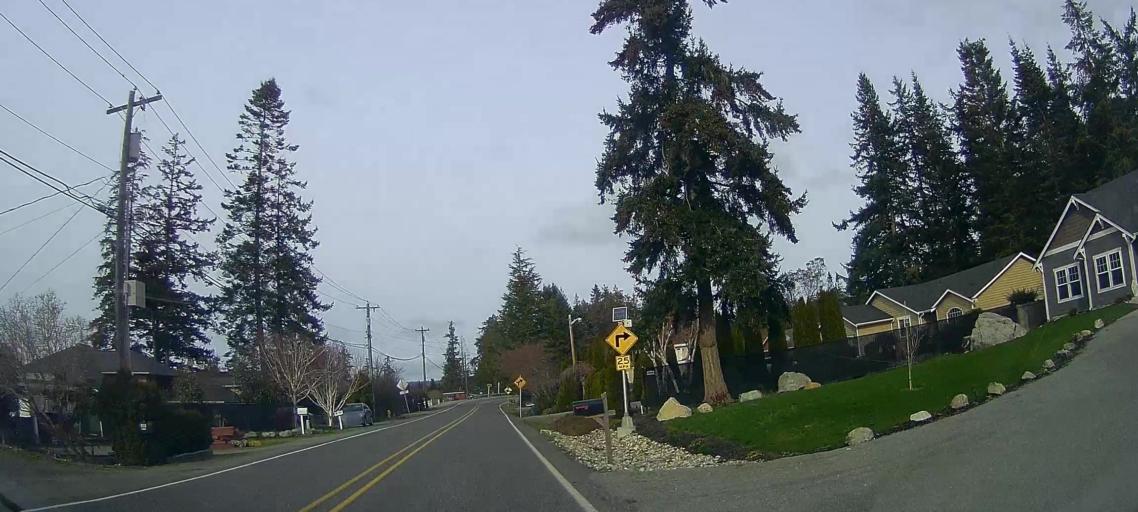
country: US
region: Washington
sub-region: Island County
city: Camano
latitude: 48.2460
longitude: -122.5208
